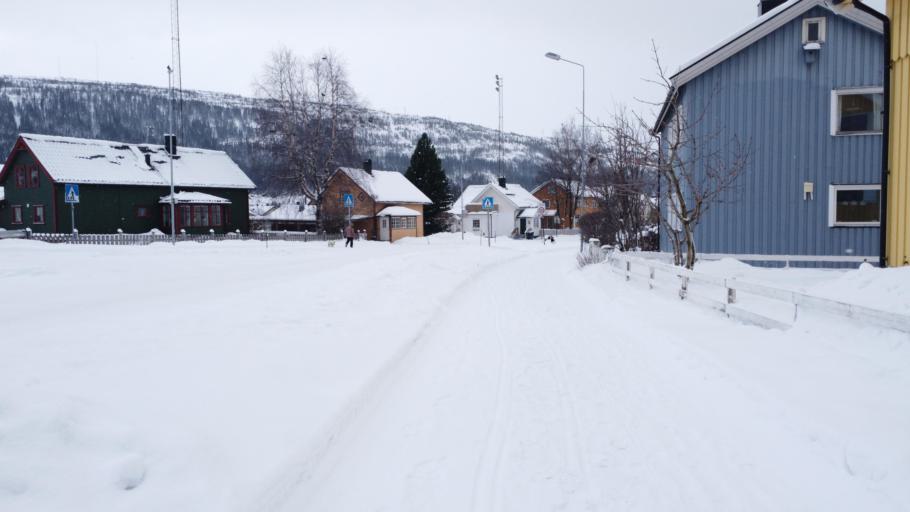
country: NO
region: Nordland
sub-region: Rana
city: Mo i Rana
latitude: 66.3131
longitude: 14.1512
